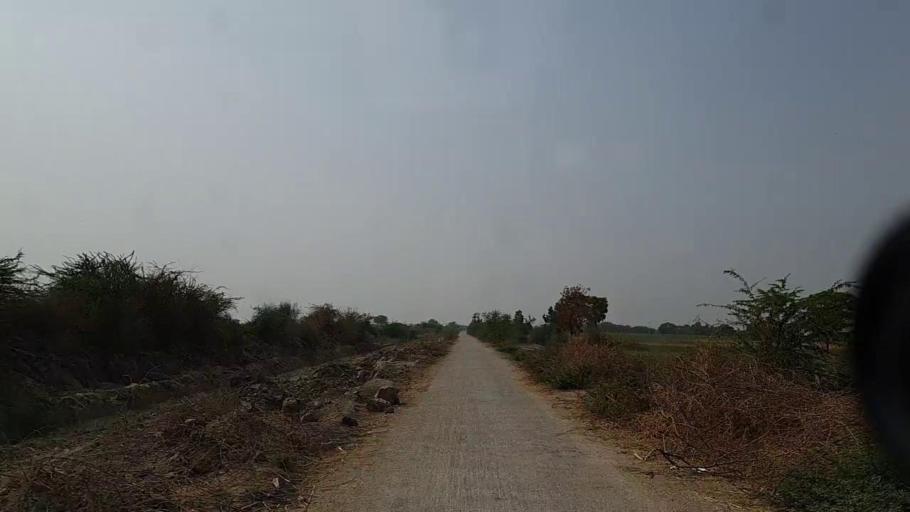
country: PK
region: Sindh
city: Naukot
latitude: 24.7723
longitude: 69.3132
